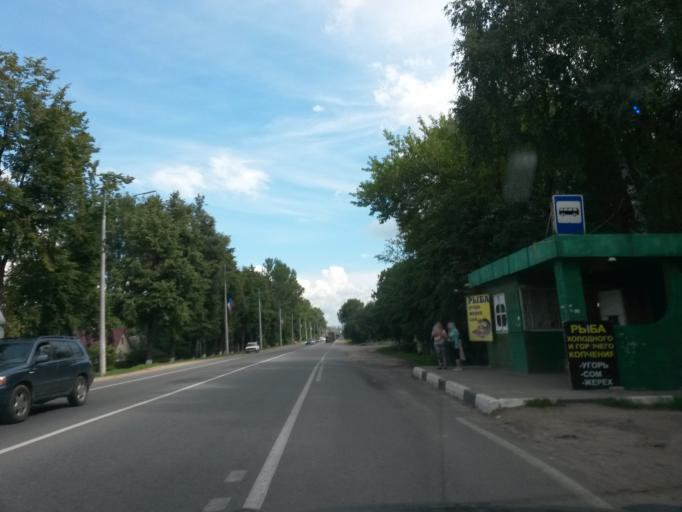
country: RU
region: Jaroslavl
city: Pereslavl'-Zalesskiy
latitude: 56.7157
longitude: 38.8214
